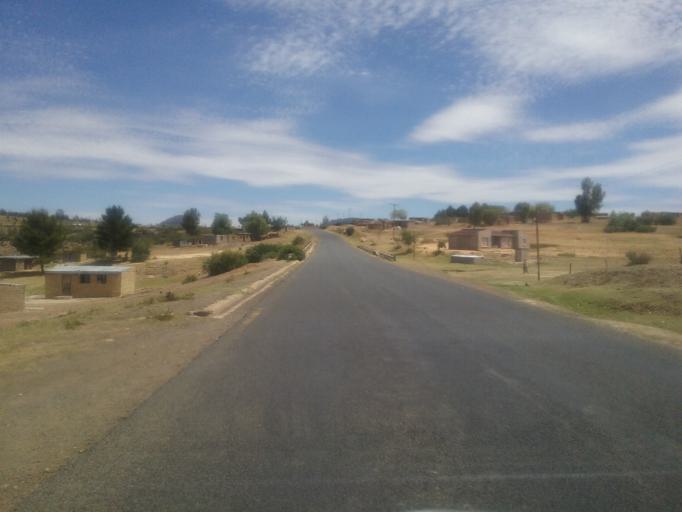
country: LS
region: Mafeteng
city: Mafeteng
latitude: -29.9936
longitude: 27.3362
